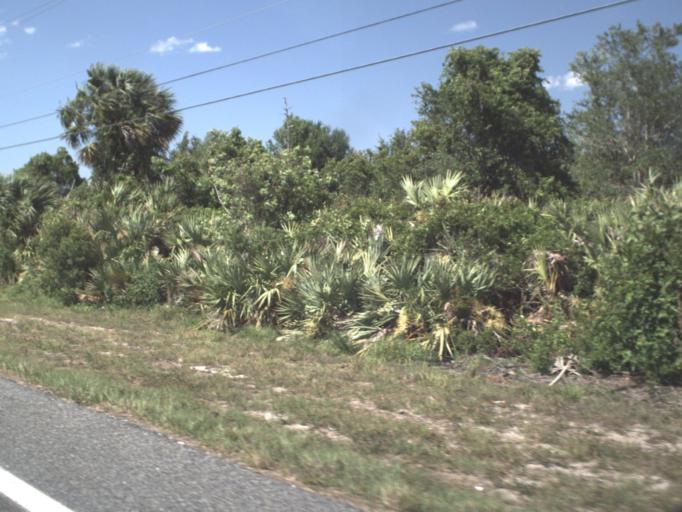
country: US
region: Florida
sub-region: Volusia County
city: Oak Hill
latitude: 28.7779
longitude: -80.8810
